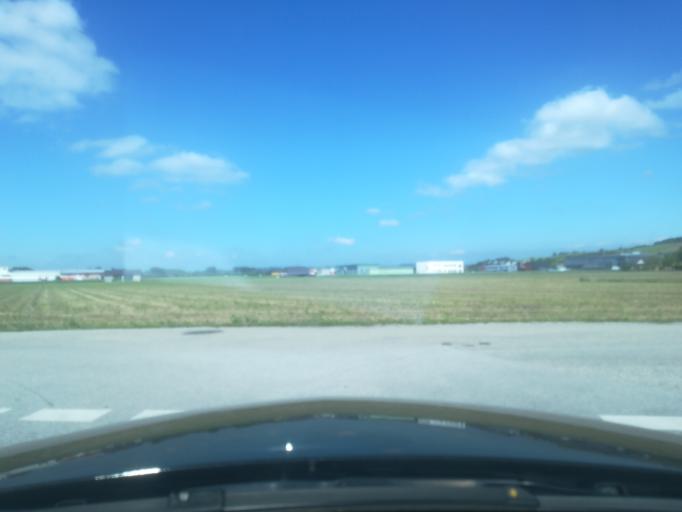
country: AT
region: Upper Austria
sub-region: Politischer Bezirk Perg
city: Perg
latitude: 48.2434
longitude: 14.6241
